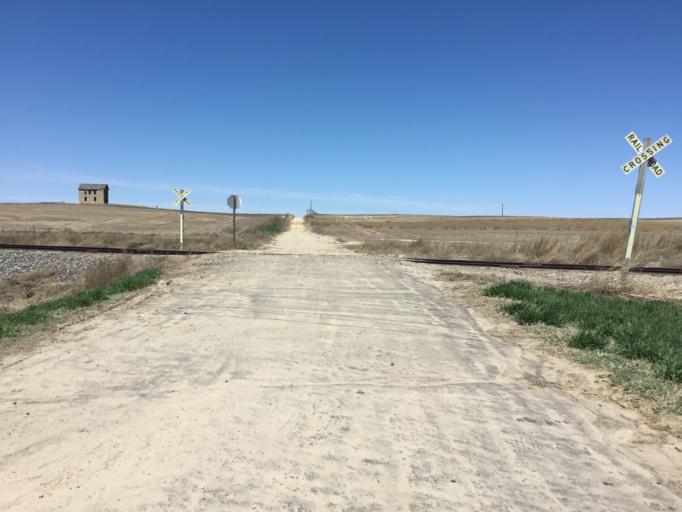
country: US
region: Kansas
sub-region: Phillips County
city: Phillipsburg
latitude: 39.7782
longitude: -99.4030
